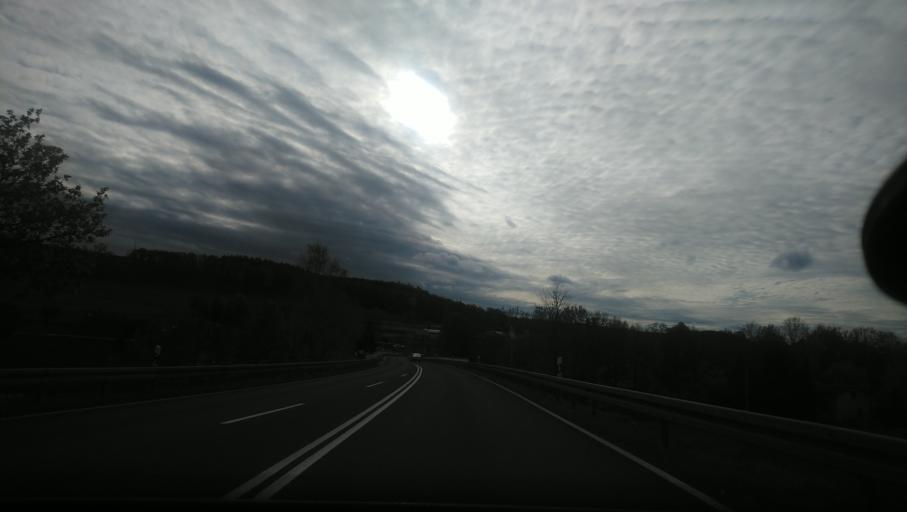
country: DE
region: Saxony
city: Dorfchemnitz
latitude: 50.6476
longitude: 12.8261
